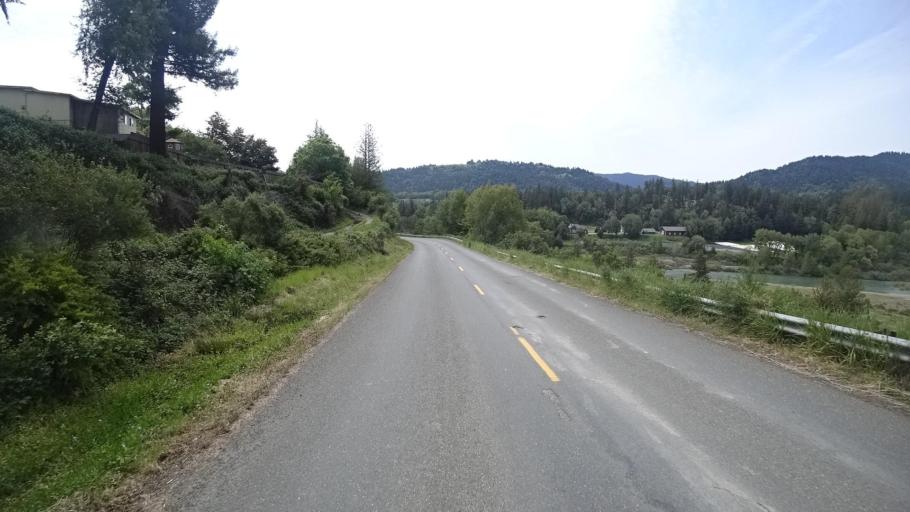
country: US
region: California
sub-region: Humboldt County
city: Redway
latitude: 40.0975
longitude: -123.7989
